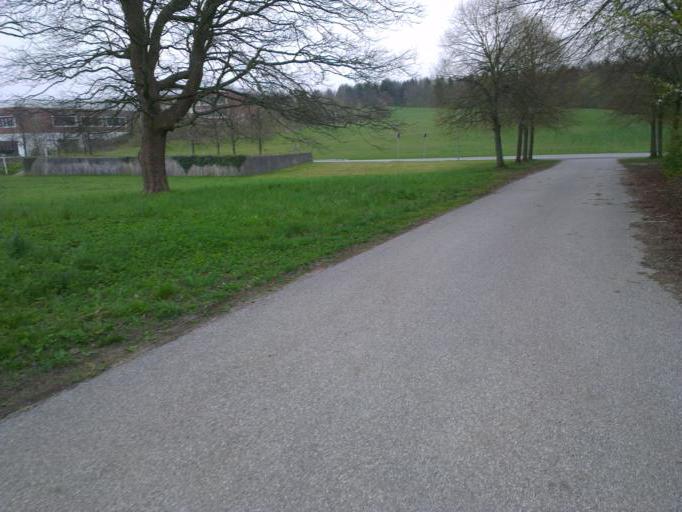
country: DK
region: Capital Region
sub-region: Frederikssund Kommune
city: Frederikssund
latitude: 55.8464
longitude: 12.0820
